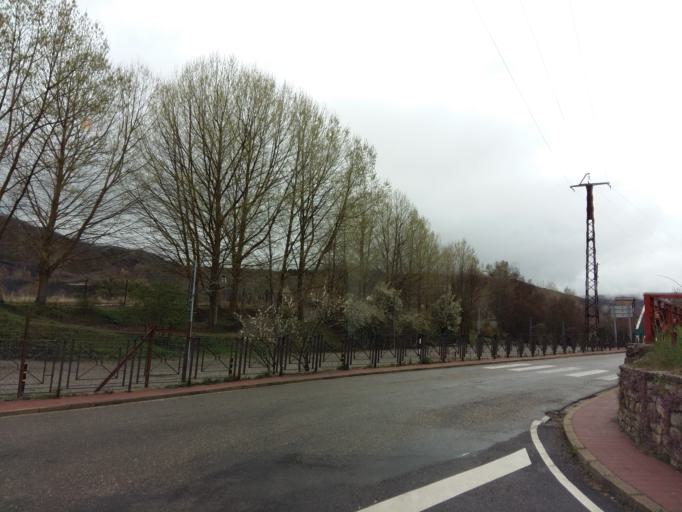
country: ES
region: Castille and Leon
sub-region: Provincia de Palencia
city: Barruelo de Santullan
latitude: 42.9022
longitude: -4.2877
